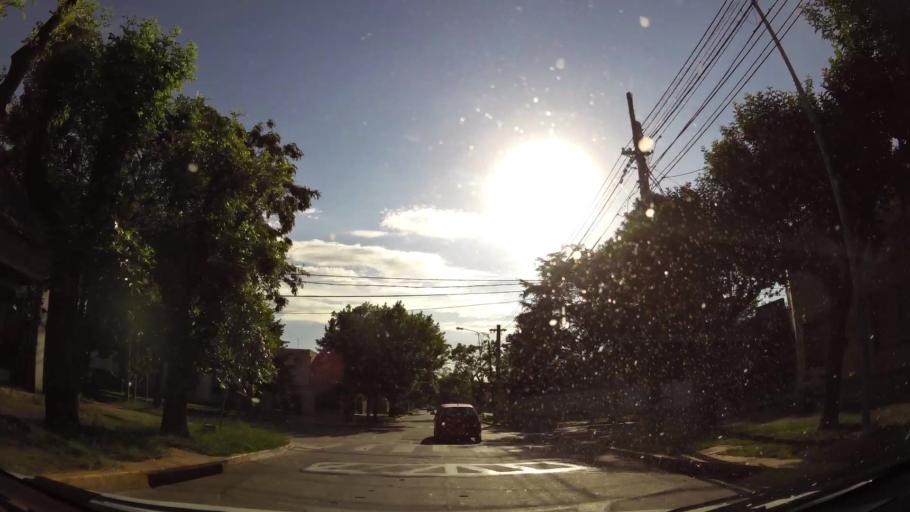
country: AR
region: Buenos Aires
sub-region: Partido de Merlo
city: Merlo
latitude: -34.6713
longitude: -58.7294
